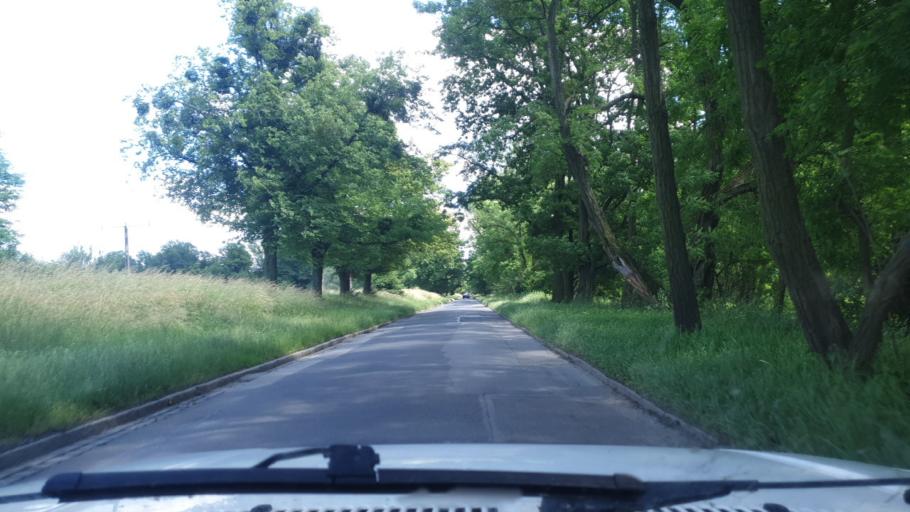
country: PL
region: Lower Silesian Voivodeship
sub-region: Powiat wroclawski
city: Radwanice
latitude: 51.0942
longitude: 17.0831
